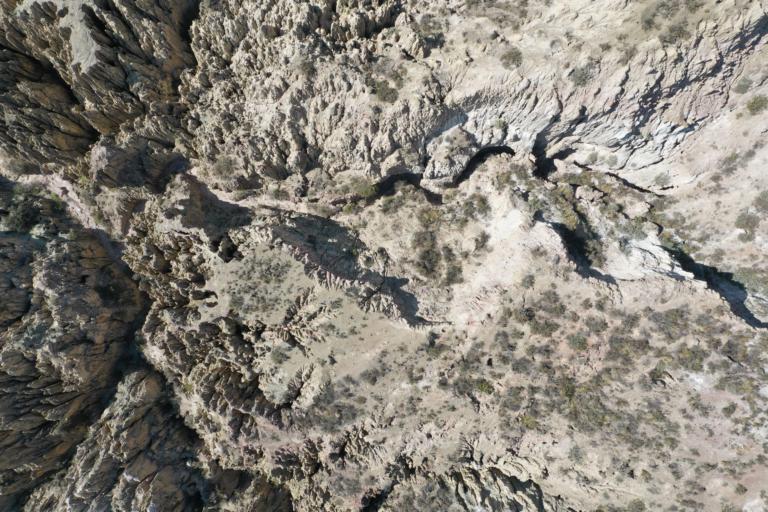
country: BO
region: La Paz
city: La Paz
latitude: -16.5630
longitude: -68.1299
